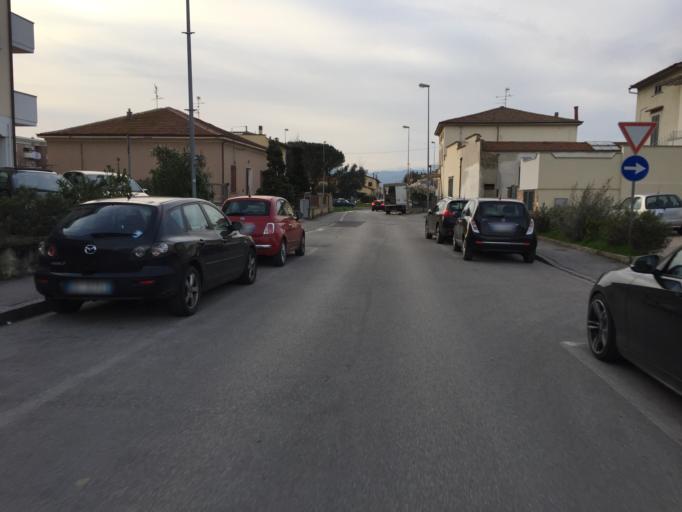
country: IT
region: Tuscany
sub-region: Provincia di Prato
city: Fornacelle
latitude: 43.8891
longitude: 11.0507
